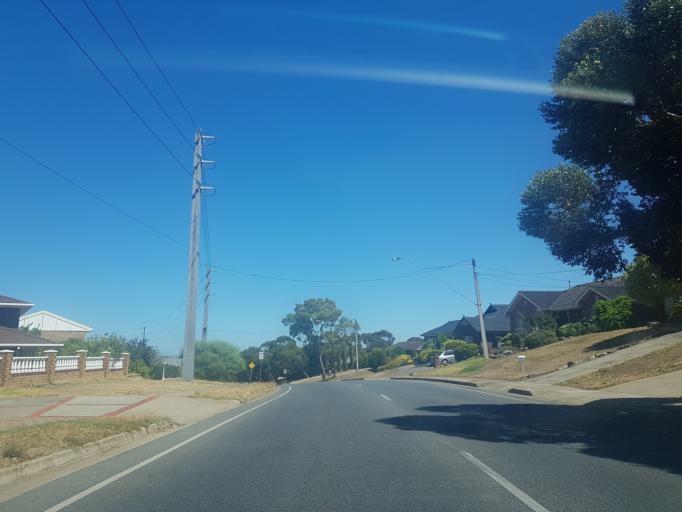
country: AU
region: South Australia
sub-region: Tea Tree Gully
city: Modbury
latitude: -34.8184
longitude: 138.6628
